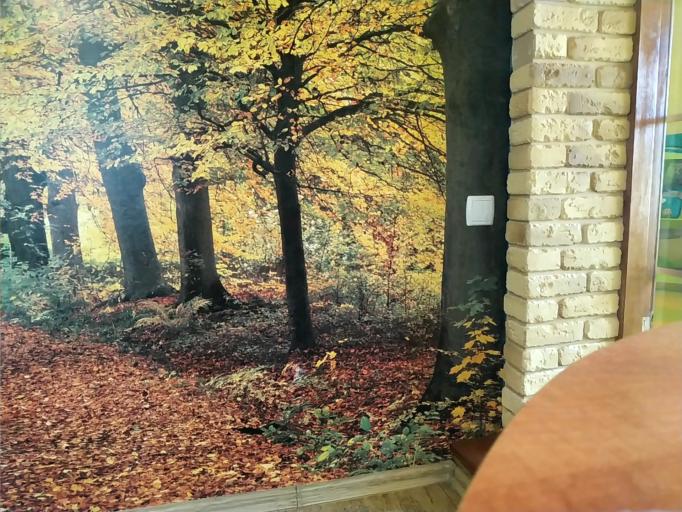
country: RU
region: Arkhangelskaya
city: Onega
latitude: 63.7075
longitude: 38.0877
